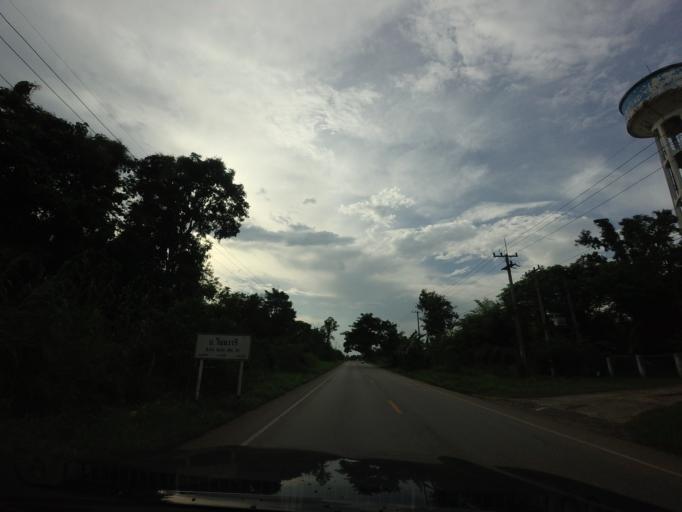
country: TH
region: Changwat Udon Thani
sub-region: Amphoe Ban Phue
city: Ban Phue
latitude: 17.7023
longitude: 102.4374
